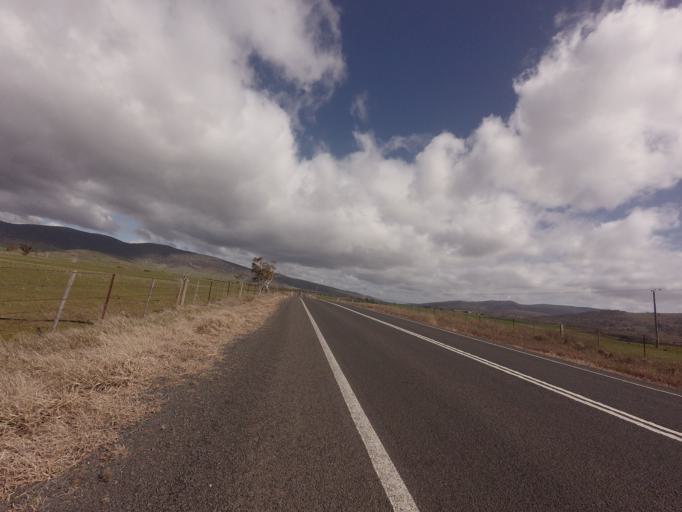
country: AU
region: Tasmania
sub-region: Northern Midlands
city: Evandale
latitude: -41.8065
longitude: 147.6794
